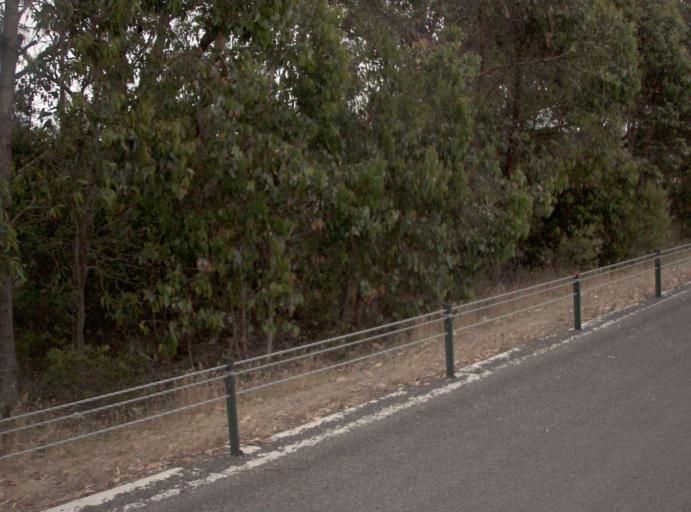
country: AU
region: Victoria
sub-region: Latrobe
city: Morwell
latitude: -38.2178
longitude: 146.3273
